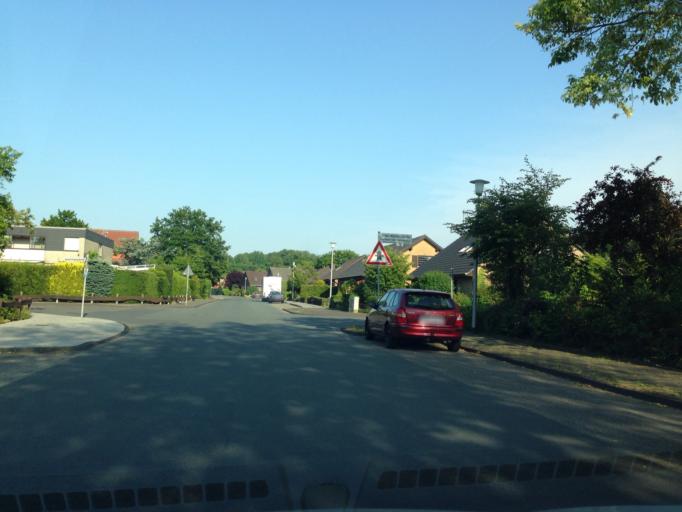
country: DE
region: North Rhine-Westphalia
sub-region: Regierungsbezirk Munster
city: Muenster
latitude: 51.9917
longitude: 7.5493
